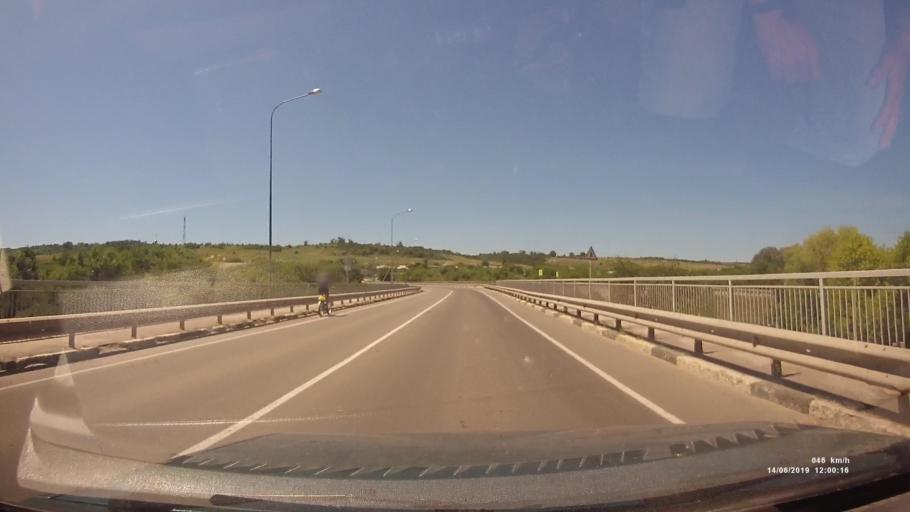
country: RU
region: Rostov
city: Kazanskaya
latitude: 49.7898
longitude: 41.1294
